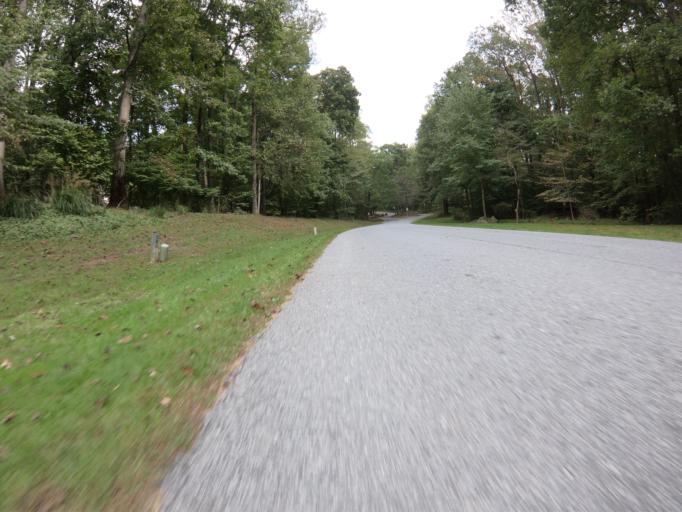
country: US
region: Maryland
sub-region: Howard County
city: Columbia
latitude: 39.2569
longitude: -76.8709
